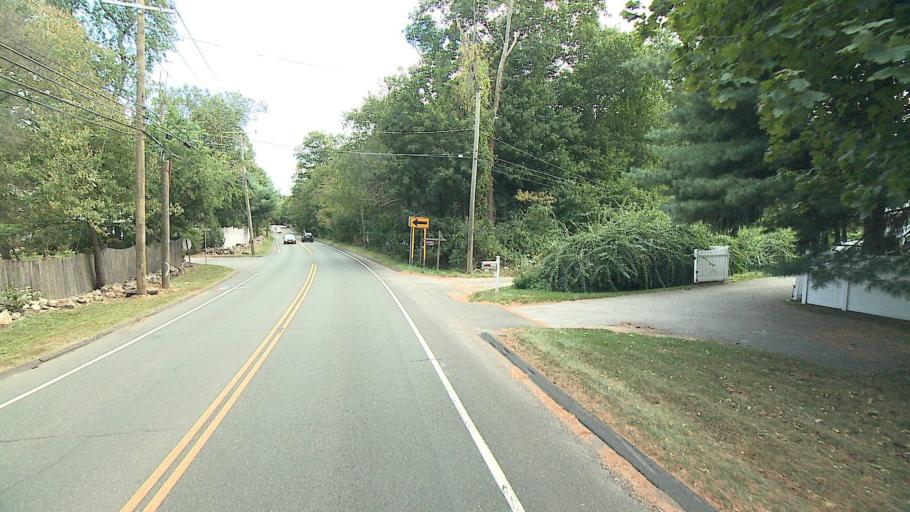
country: US
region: Connecticut
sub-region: Fairfield County
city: Westport
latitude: 41.1689
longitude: -73.3863
